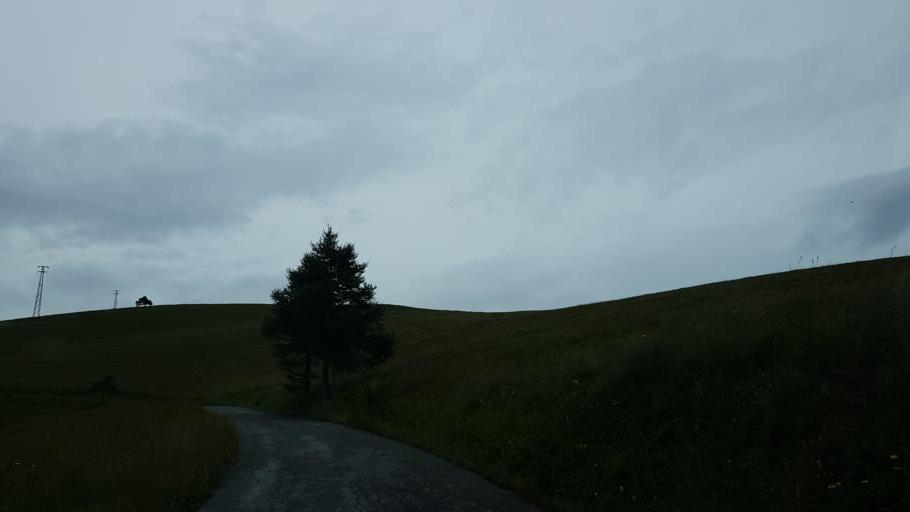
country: IT
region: Piedmont
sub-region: Provincia di Cuneo
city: Serre
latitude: 44.5305
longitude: 7.1136
